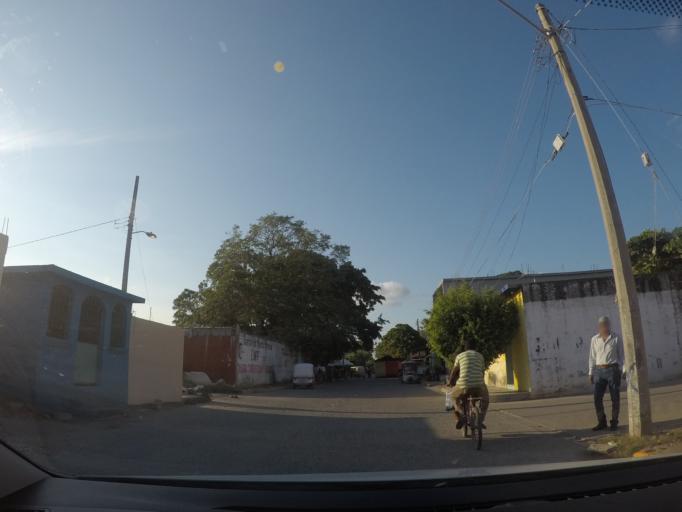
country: MX
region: Oaxaca
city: Juchitan de Zaragoza
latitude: 16.4354
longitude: -95.0303
